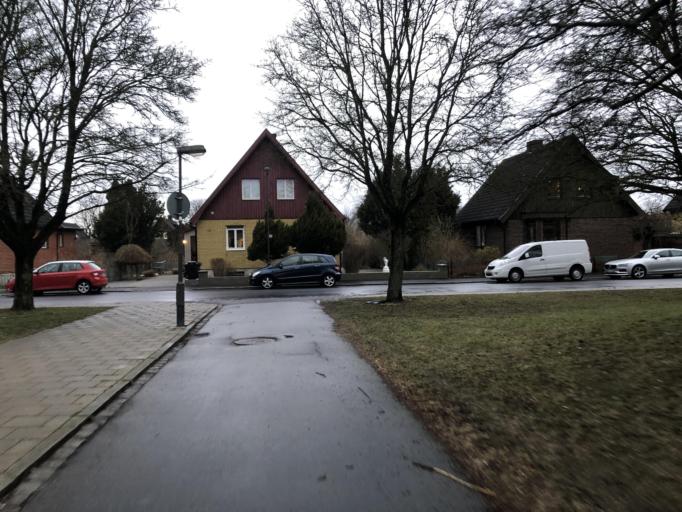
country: SE
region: Skane
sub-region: Burlovs Kommun
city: Arloev
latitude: 55.5848
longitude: 13.0618
